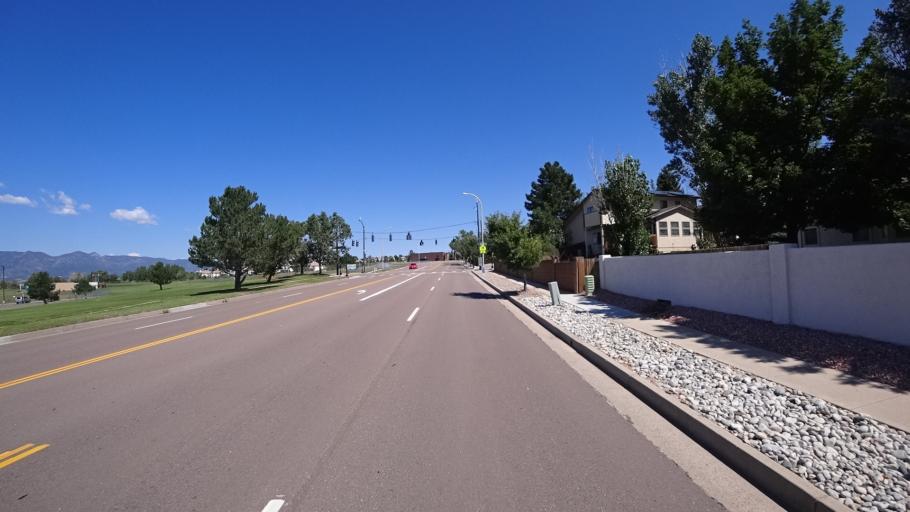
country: US
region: Colorado
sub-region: El Paso County
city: Black Forest
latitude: 38.9507
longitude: -104.7708
